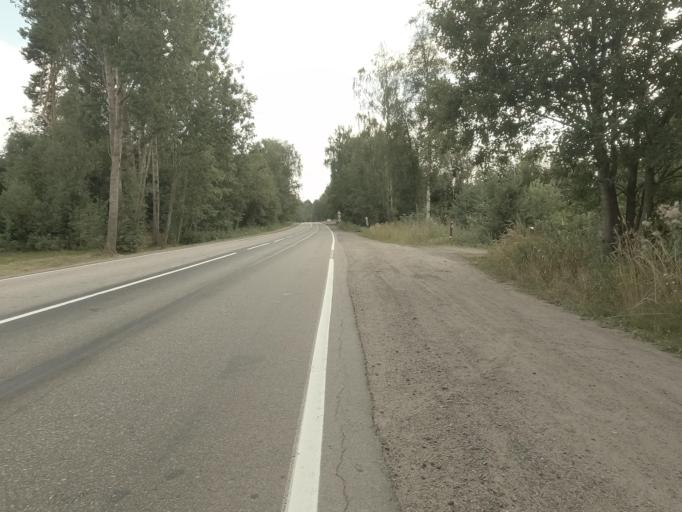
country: RU
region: Leningrad
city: Kamennogorsk
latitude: 60.8626
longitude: 28.9712
